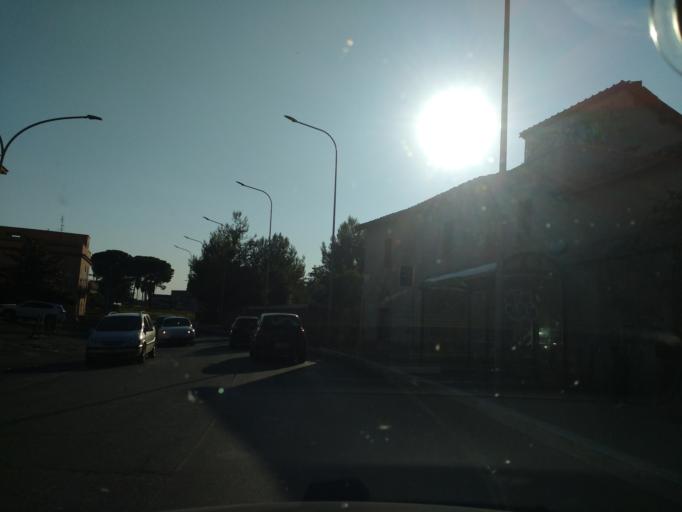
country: IT
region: Latium
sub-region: Citta metropolitana di Roma Capitale
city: Villa Adriana
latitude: 41.9564
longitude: 12.7706
